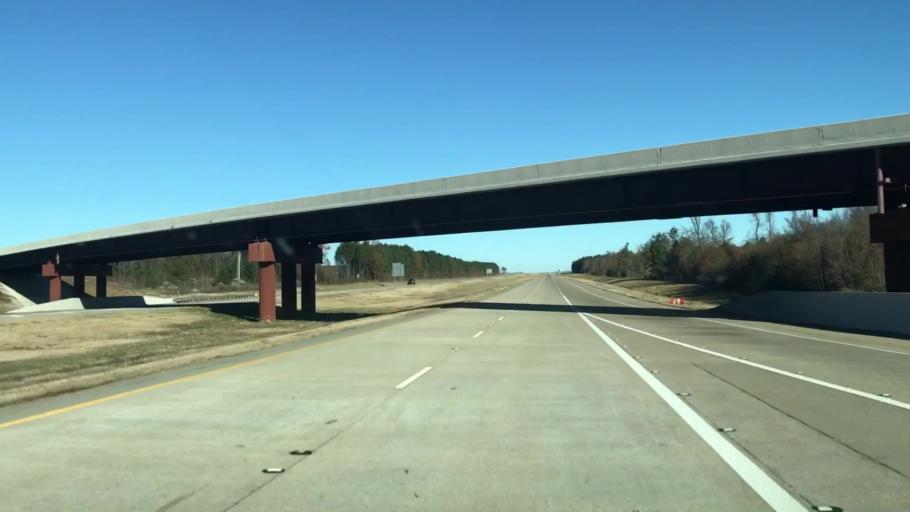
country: US
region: Louisiana
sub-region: Caddo Parish
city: Blanchard
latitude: 32.5999
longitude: -93.8322
